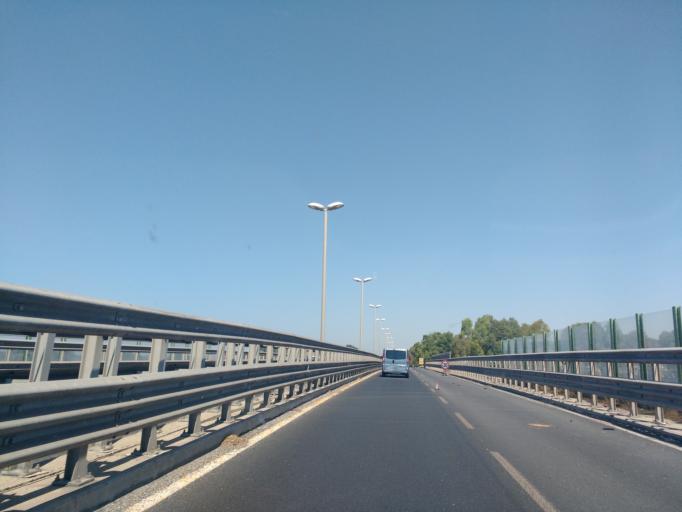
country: IT
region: Latium
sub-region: Citta metropolitana di Roma Capitale
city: Fiumicino-Isola Sacra
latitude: 41.7731
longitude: 12.2558
